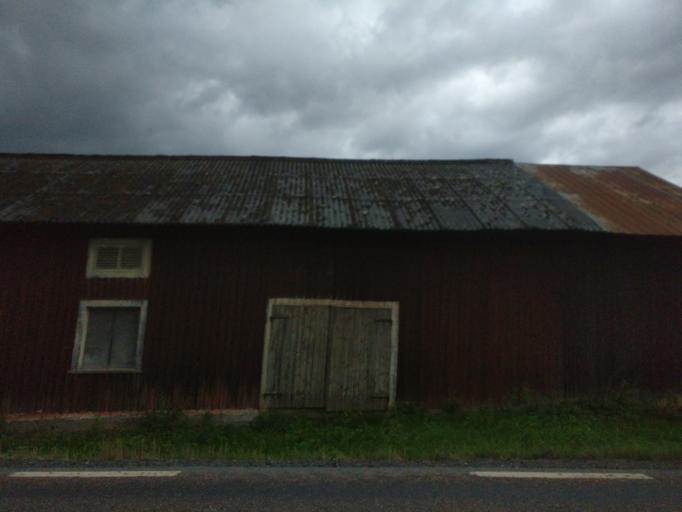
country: SE
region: Vaermland
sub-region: Torsby Kommun
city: Torsby
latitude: 60.7069
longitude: 12.8946
